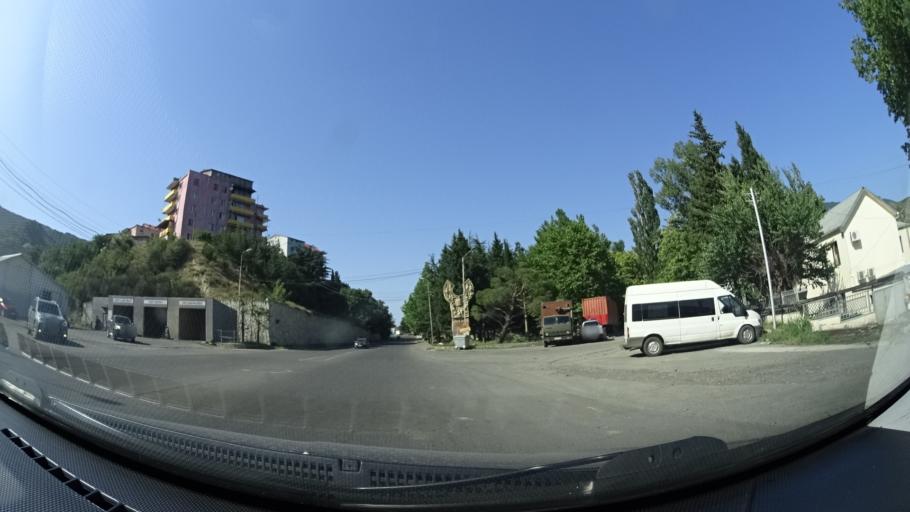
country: GE
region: Mtskheta-Mtianeti
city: Mtskheta
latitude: 41.8598
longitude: 44.7227
